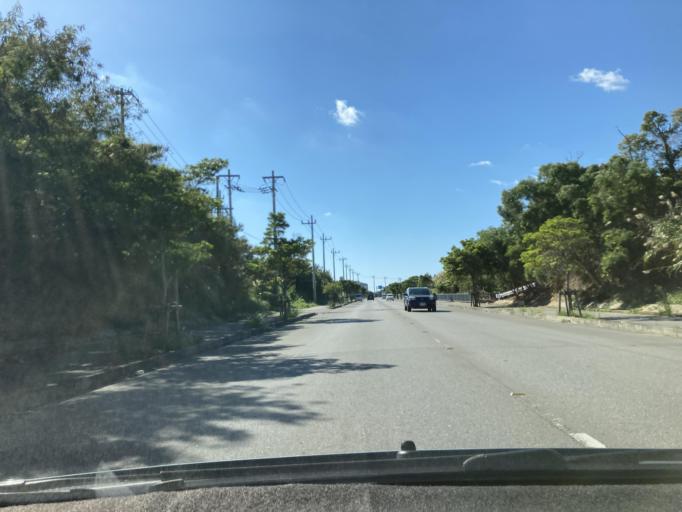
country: JP
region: Okinawa
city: Gushikawa
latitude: 26.3778
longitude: 127.8339
